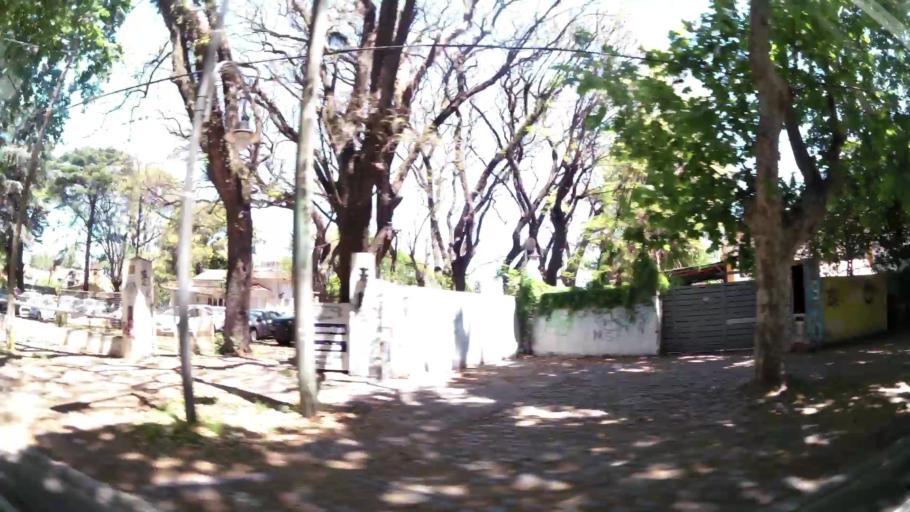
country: AR
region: Buenos Aires
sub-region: Partido de San Isidro
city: San Isidro
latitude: -34.4491
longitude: -58.5356
